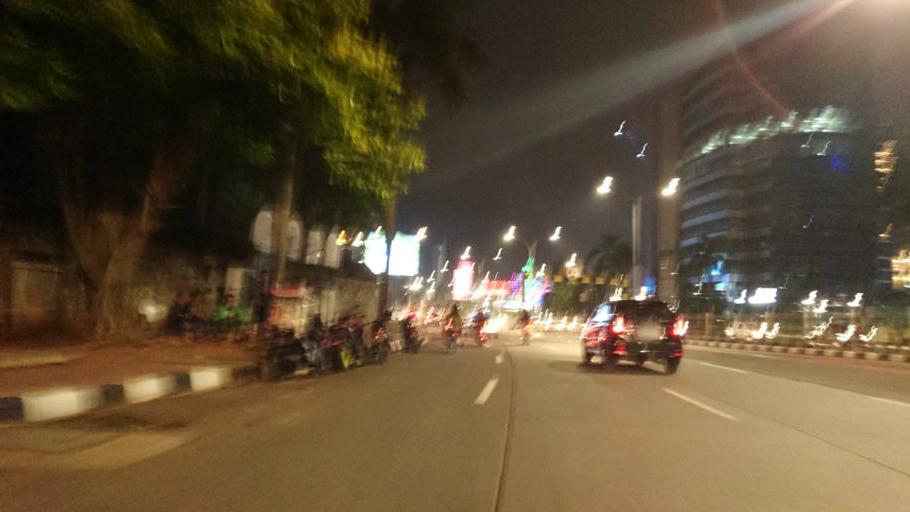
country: ID
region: Banten
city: South Tangerang
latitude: -6.2616
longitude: 106.7823
